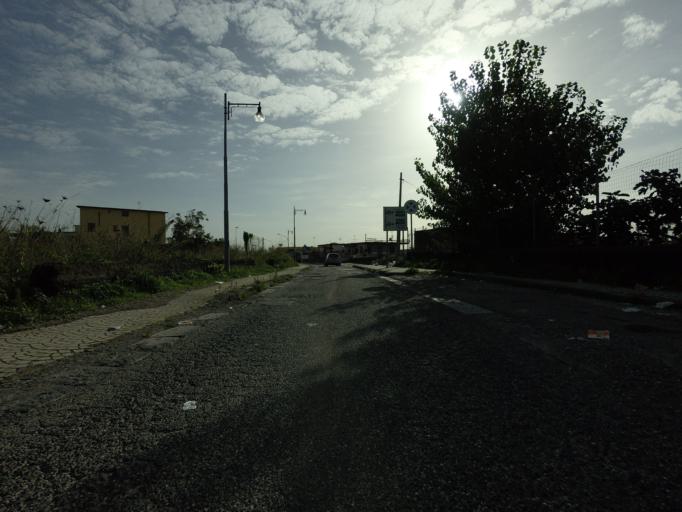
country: IT
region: Campania
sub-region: Provincia di Napoli
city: Ercolano
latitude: 40.8172
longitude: 14.3603
